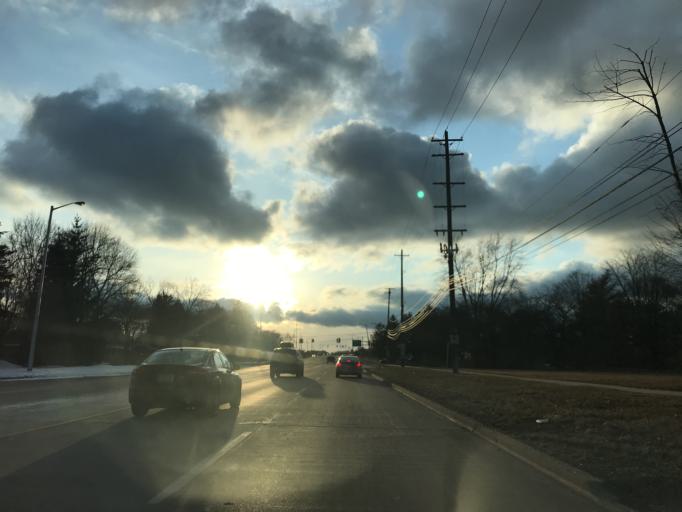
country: US
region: Michigan
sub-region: Oakland County
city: Farmington
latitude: 42.4253
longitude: -83.4179
